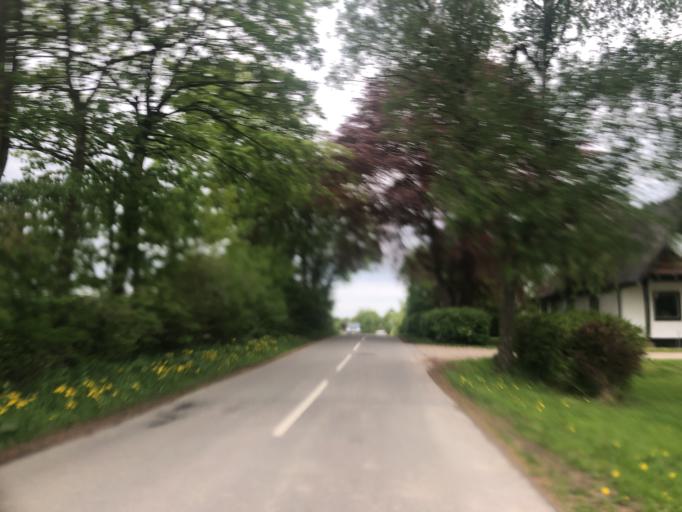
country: DK
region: Zealand
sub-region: Koge Kommune
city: Ejby
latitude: 55.4606
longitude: 12.1042
